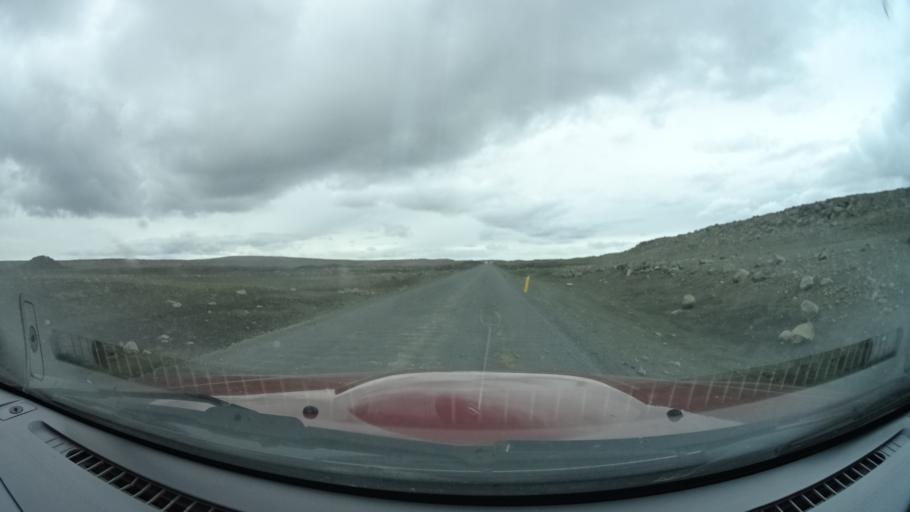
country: IS
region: Northeast
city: Husavik
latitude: 65.8134
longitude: -16.3502
